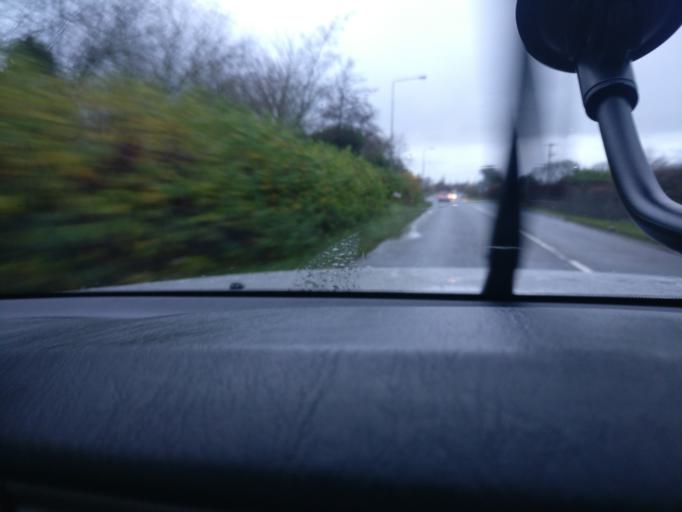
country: IE
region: Leinster
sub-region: An Iarmhi
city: Kinnegad
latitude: 53.4529
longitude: -7.1075
